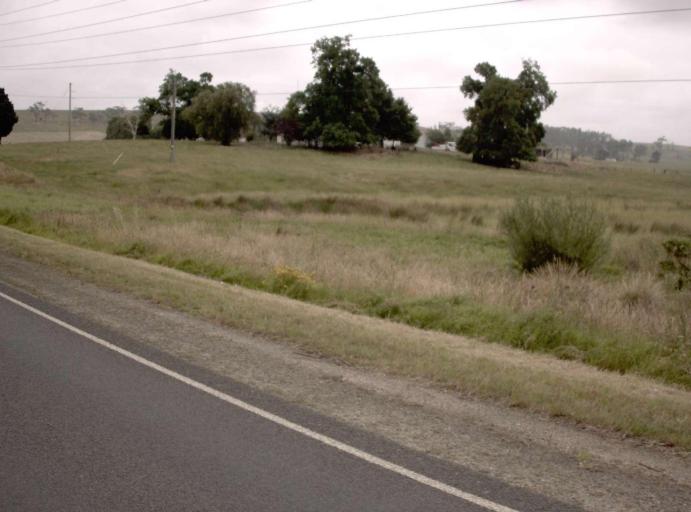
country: AU
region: Victoria
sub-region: Latrobe
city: Traralgon
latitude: -38.2501
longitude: 146.5374
